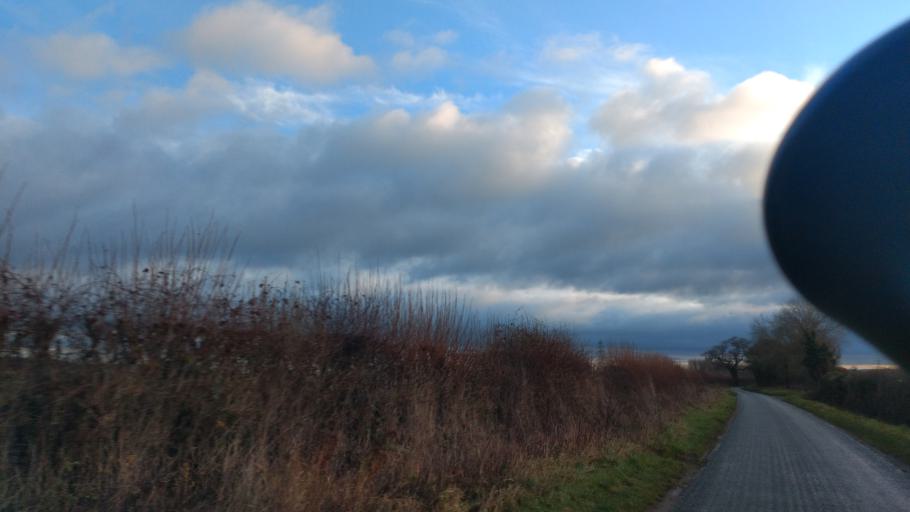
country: GB
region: England
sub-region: Wiltshire
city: Biddestone
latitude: 51.4548
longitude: -2.1894
